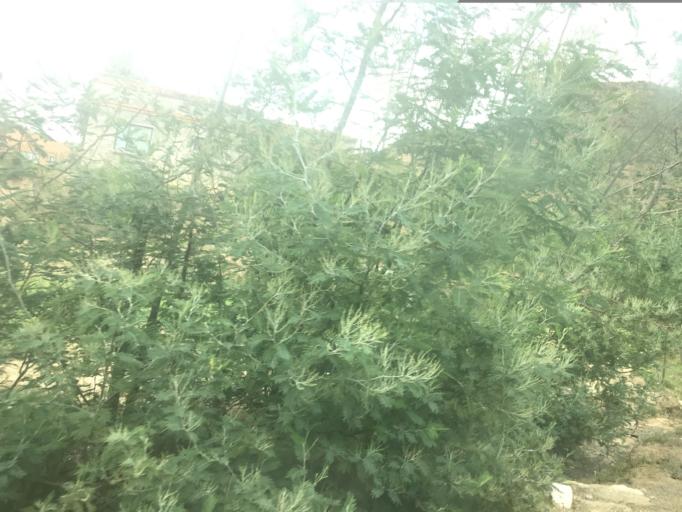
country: LS
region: Maseru
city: Nako
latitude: -29.6293
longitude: 27.5129
